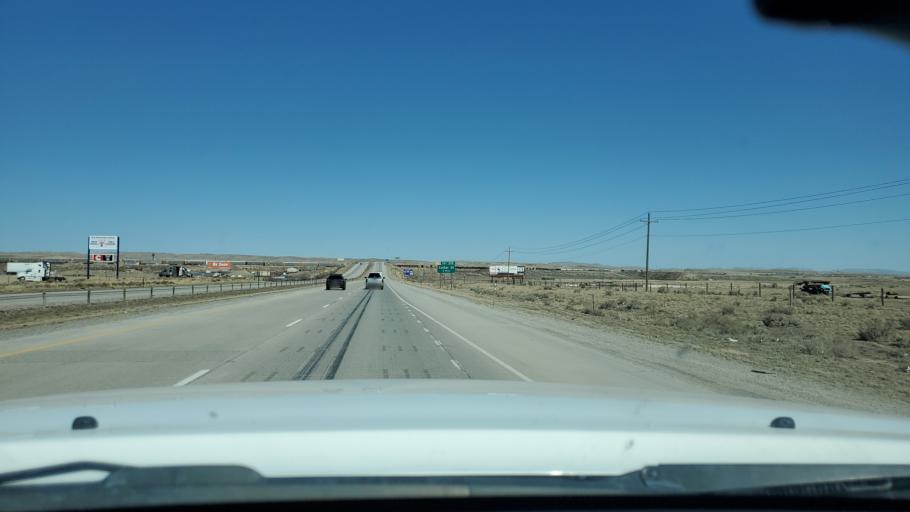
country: US
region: Wyoming
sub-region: Carbon County
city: Rawlins
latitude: 41.7815
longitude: -107.2153
